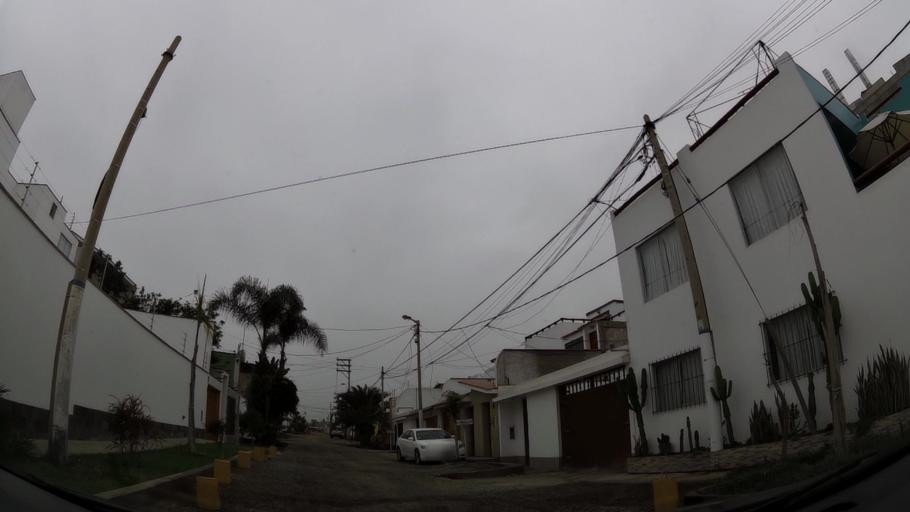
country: PE
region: Lima
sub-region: Lima
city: Punta Hermosa
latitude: -12.3323
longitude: -76.8288
